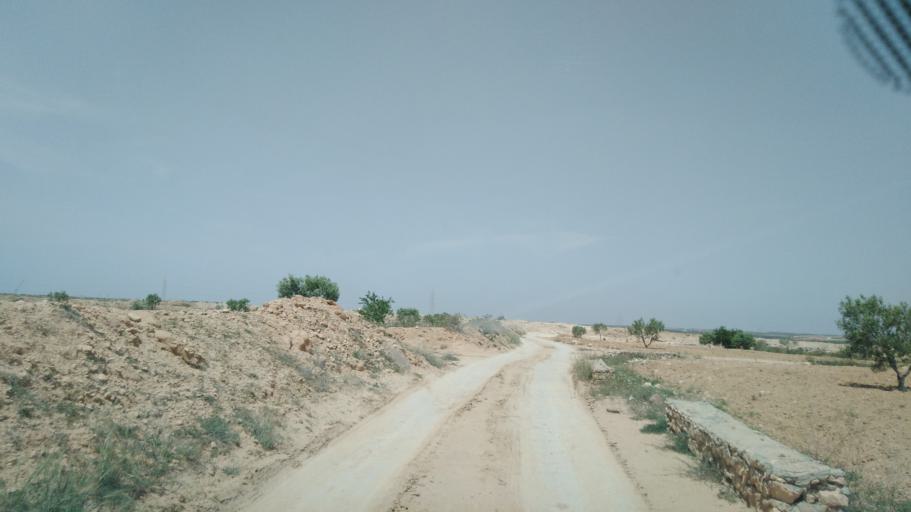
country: TN
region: Safaqis
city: Sfax
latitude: 34.7191
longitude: 10.5649
